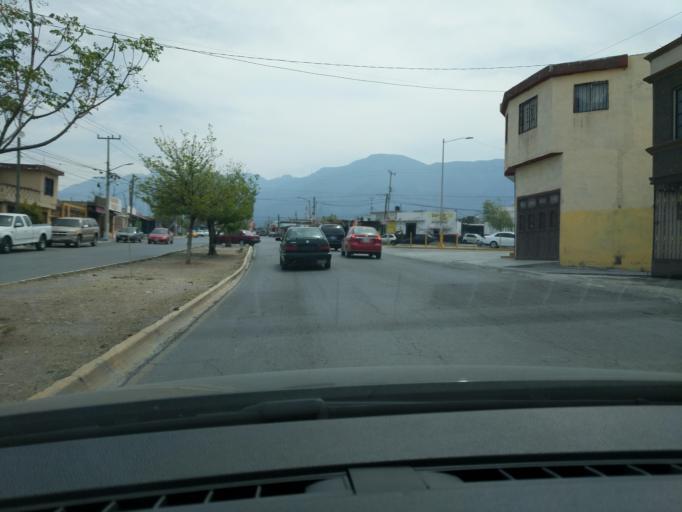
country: MX
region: Coahuila
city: Saltillo
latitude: 25.3910
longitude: -100.9807
